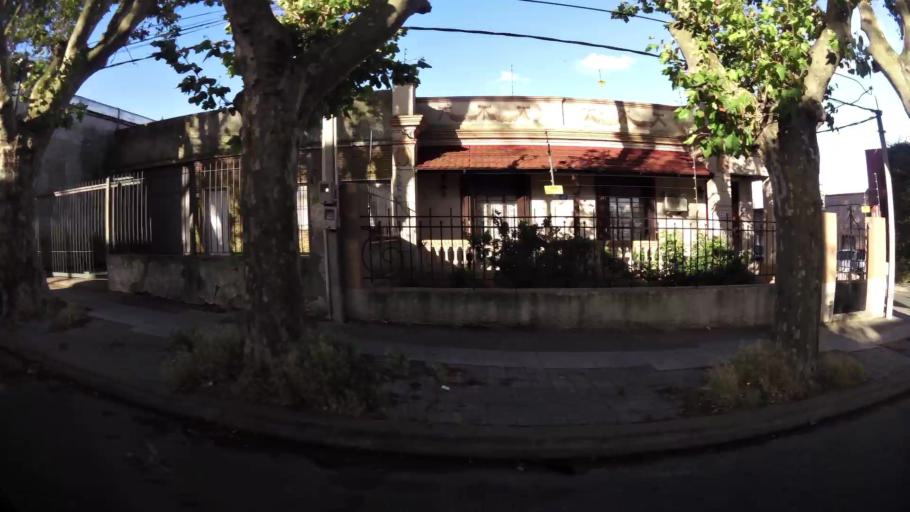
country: UY
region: Montevideo
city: Montevideo
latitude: -34.8840
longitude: -56.1336
